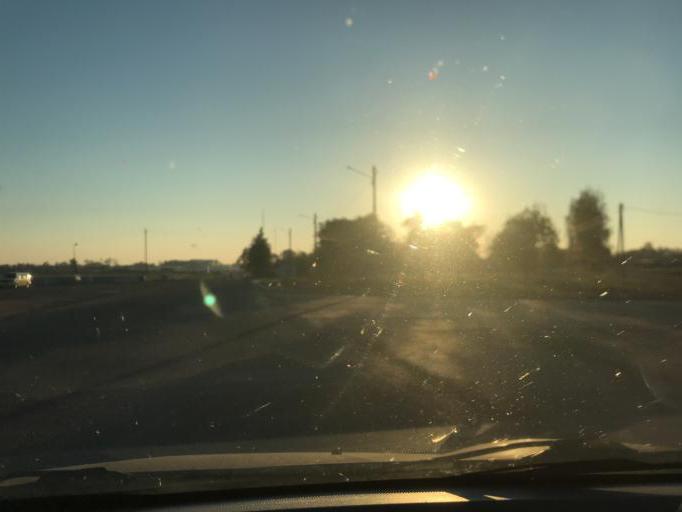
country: BY
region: Gomel
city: Brahin
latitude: 51.8091
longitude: 30.2824
